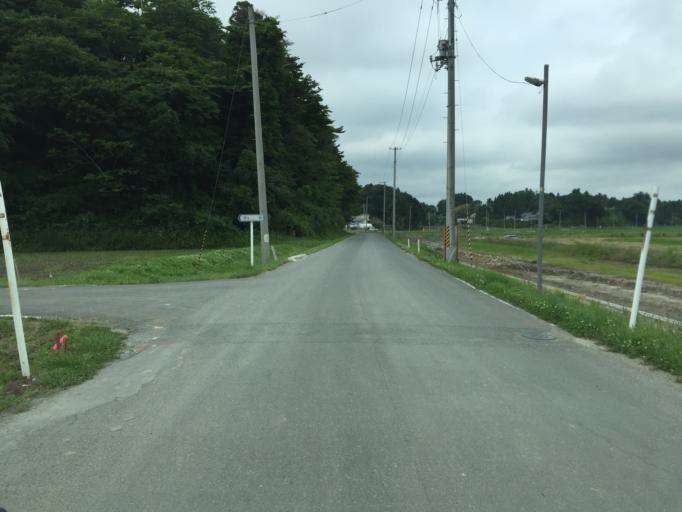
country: JP
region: Fukushima
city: Namie
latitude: 37.7302
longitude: 140.9778
